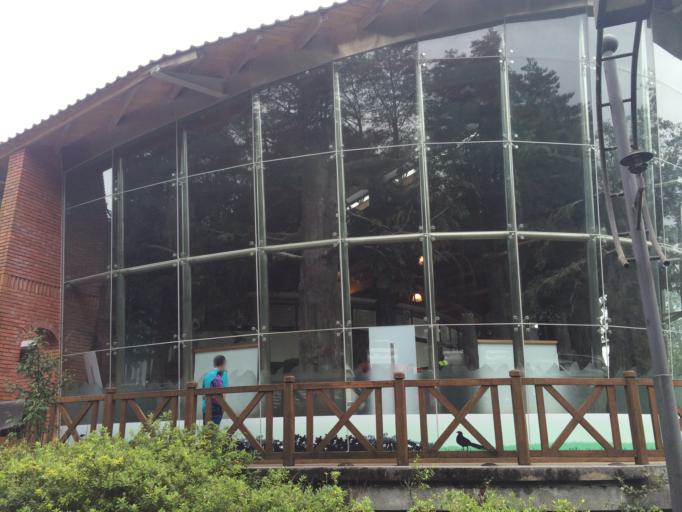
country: TW
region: Taiwan
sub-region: Miaoli
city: Miaoli
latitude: 24.5059
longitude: 121.1133
